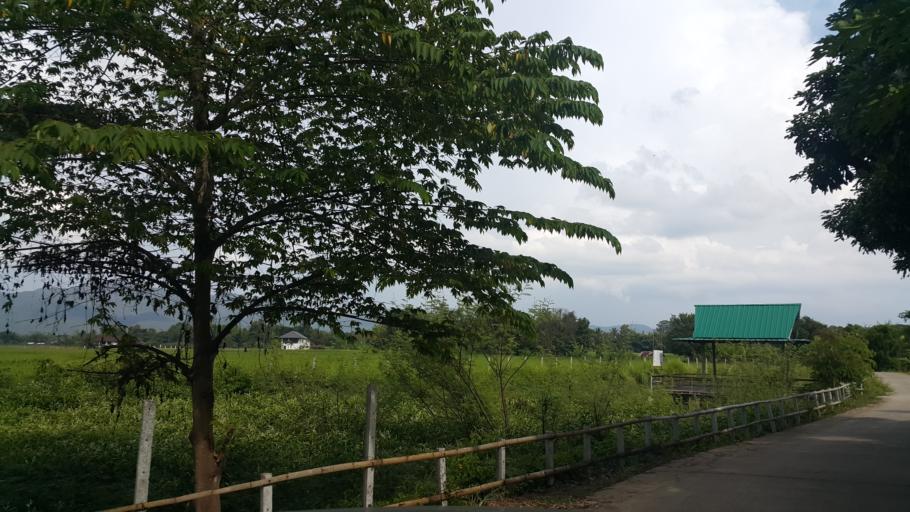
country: TH
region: Chiang Mai
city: San Sai
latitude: 18.8975
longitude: 99.1214
